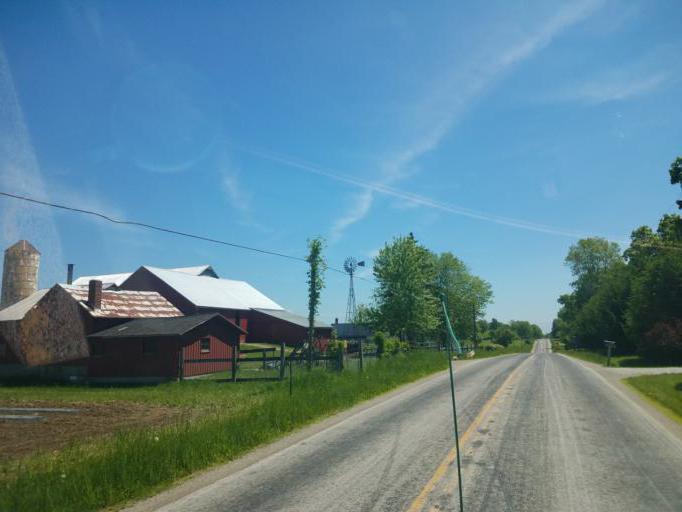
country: US
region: Ohio
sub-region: Wayne County
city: West Salem
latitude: 40.9447
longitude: -82.1830
